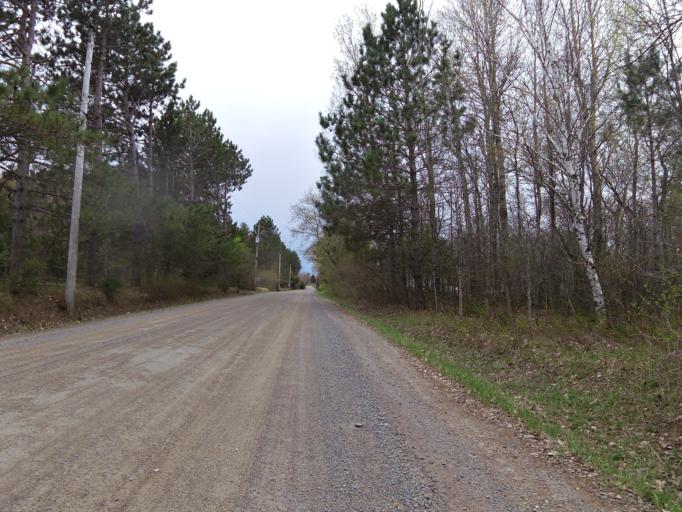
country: CA
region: Ontario
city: Hawkesbury
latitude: 45.6171
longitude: -74.5265
